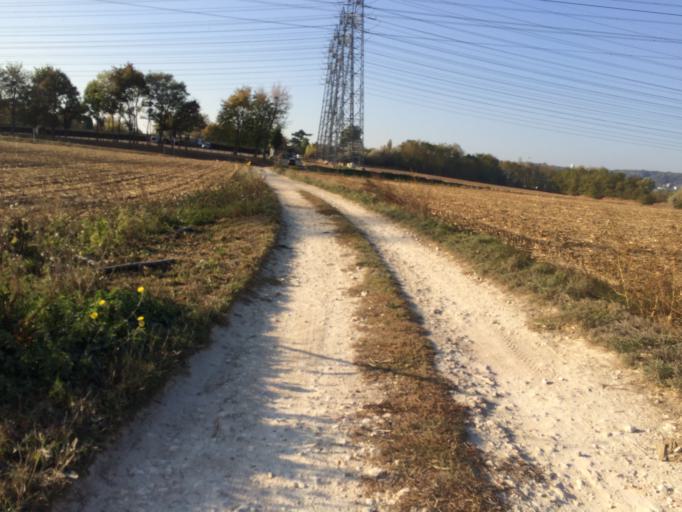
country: FR
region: Ile-de-France
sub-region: Departement de l'Essonne
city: Villebon-sur-Yvette
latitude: 48.6988
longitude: 2.2521
